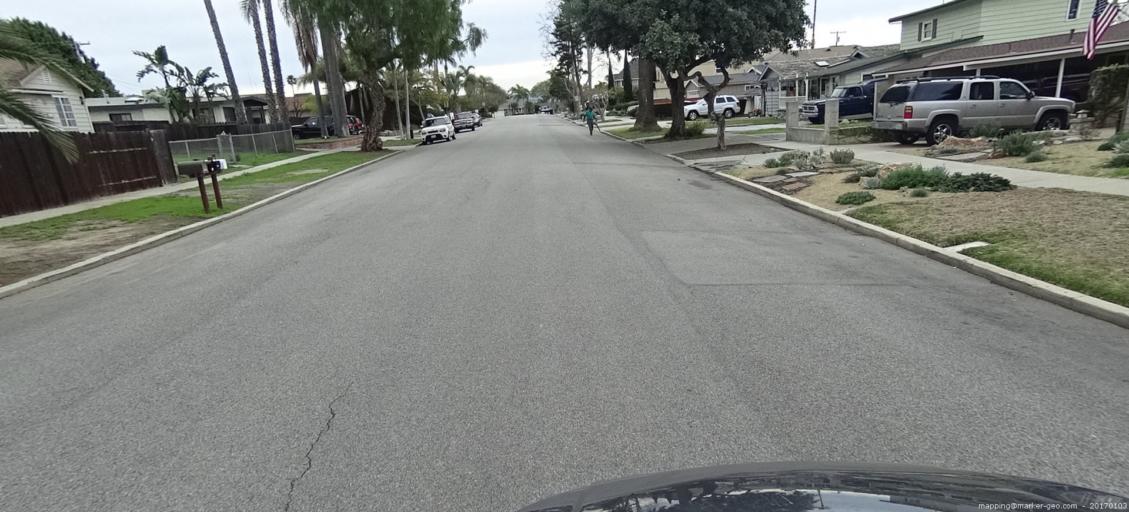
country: US
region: California
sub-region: Orange County
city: Dana Point
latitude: 33.4645
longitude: -117.6682
